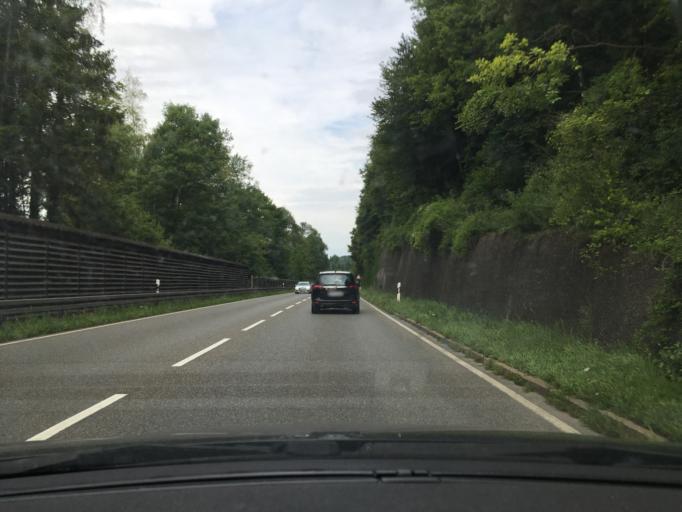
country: DE
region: Baden-Wuerttemberg
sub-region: Tuebingen Region
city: Uberlingen
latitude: 47.7549
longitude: 9.2019
